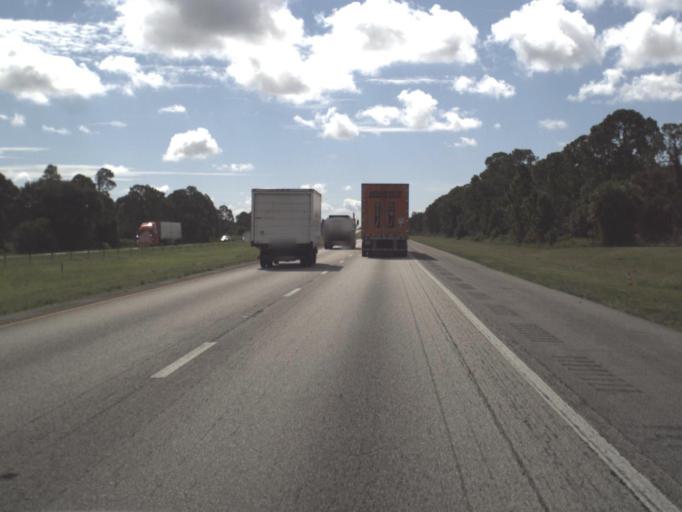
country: US
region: Florida
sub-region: Charlotte County
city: Port Charlotte
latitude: 27.0685
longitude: -82.0948
